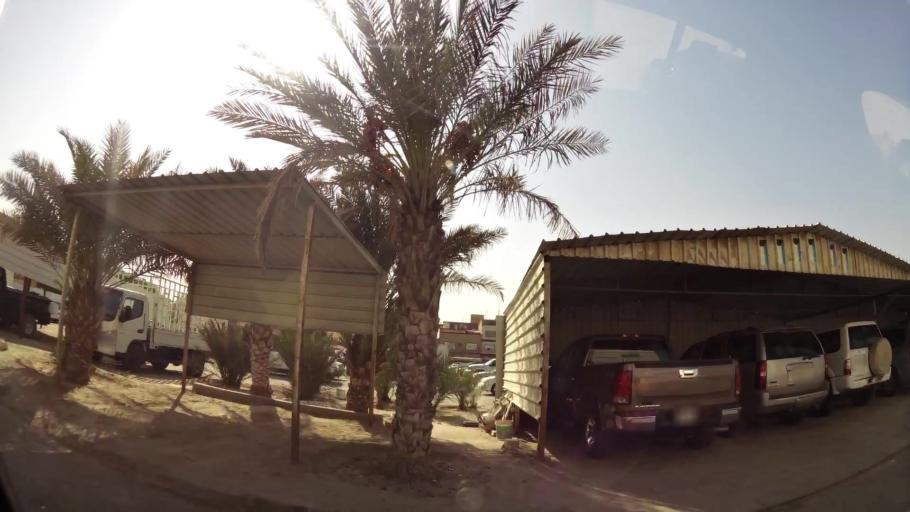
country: KW
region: Muhafazat Hawalli
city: Salwa
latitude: 29.2932
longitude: 48.0808
